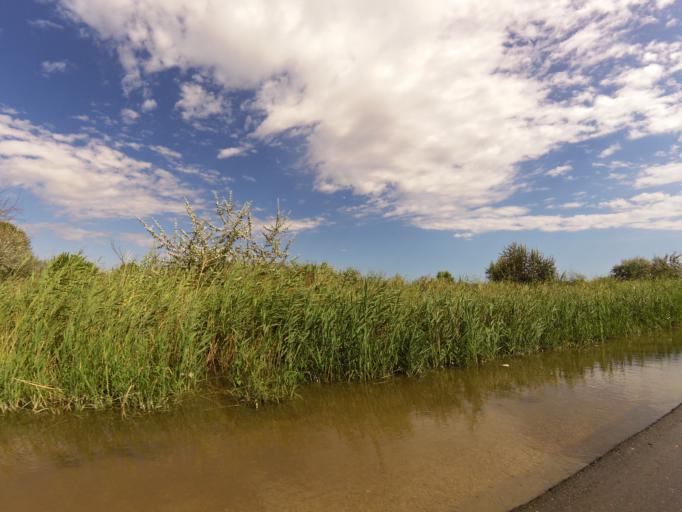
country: FR
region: Languedoc-Roussillon
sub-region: Departement du Gard
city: Le Grau-du-Roi
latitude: 43.5217
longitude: 4.1498
